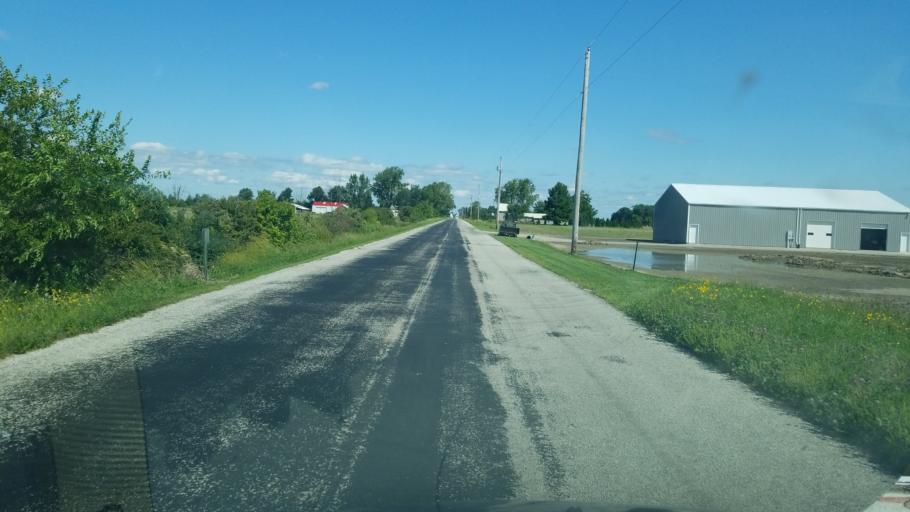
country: US
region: Ohio
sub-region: Henry County
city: Deshler
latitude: 41.2442
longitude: -83.8425
